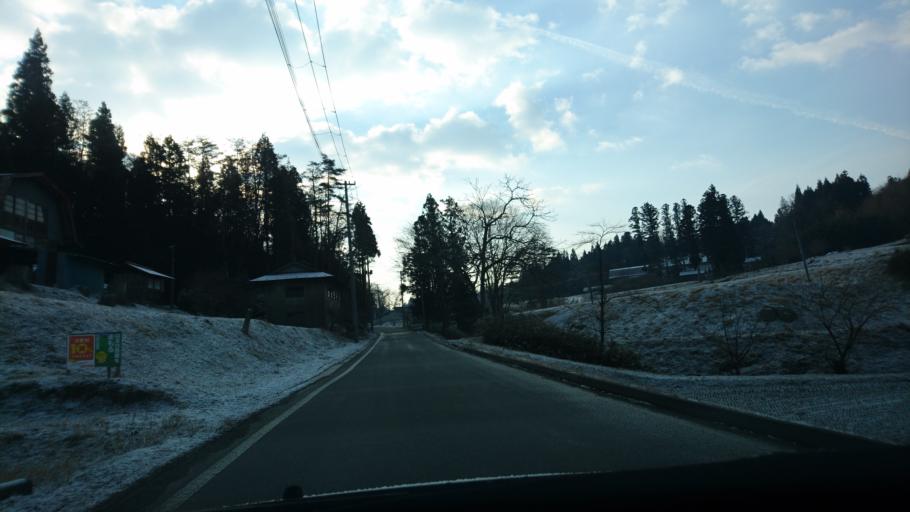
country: JP
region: Iwate
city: Ichinoseki
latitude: 38.9161
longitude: 141.3625
